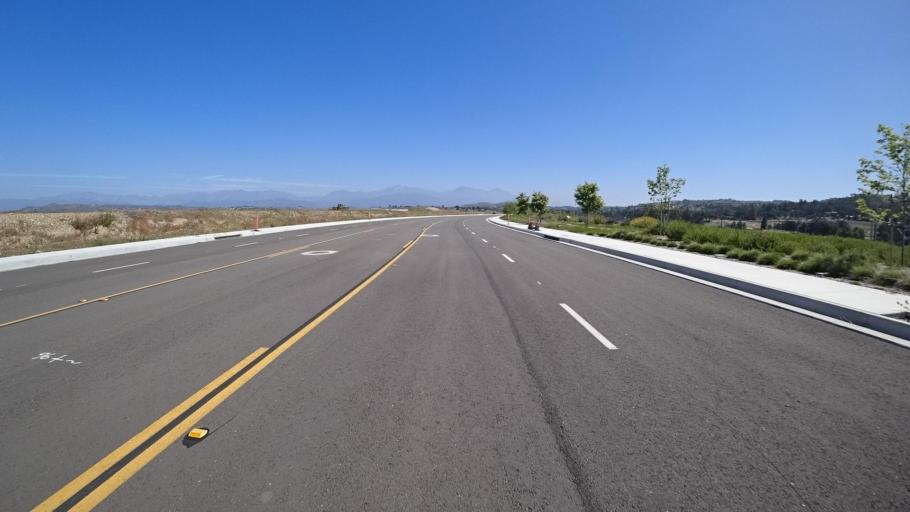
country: US
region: California
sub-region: Los Angeles County
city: Diamond Bar
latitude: 34.0063
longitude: -117.8309
